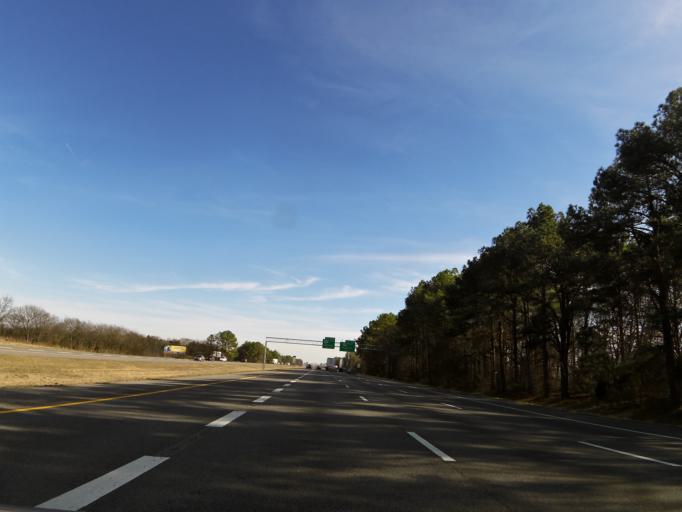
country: US
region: Tennessee
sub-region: Rutherford County
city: Smyrna
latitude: 35.9006
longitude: -86.4945
